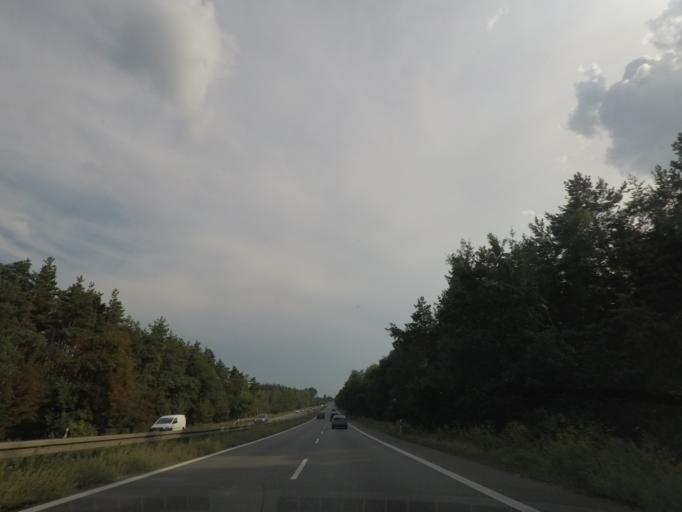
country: PL
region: Silesian Voivodeship
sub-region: Dabrowa Gornicza
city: Dabrowa Gornicza
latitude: 50.3531
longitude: 19.2504
